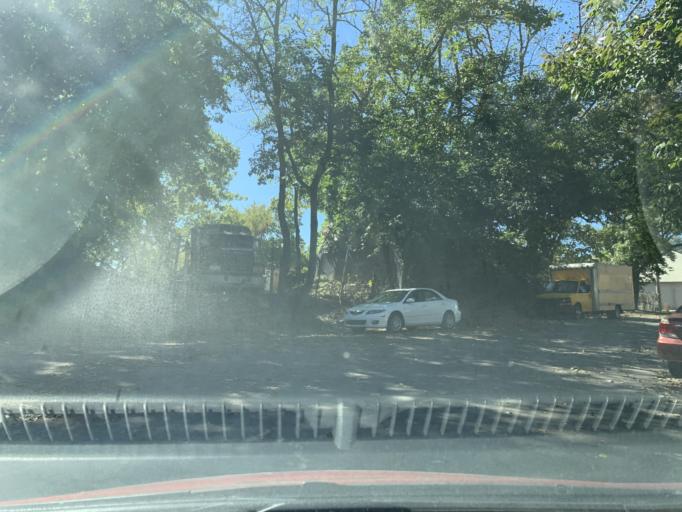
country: US
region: Indiana
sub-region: Clark County
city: Jeffersonville
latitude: 38.2545
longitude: -85.7134
